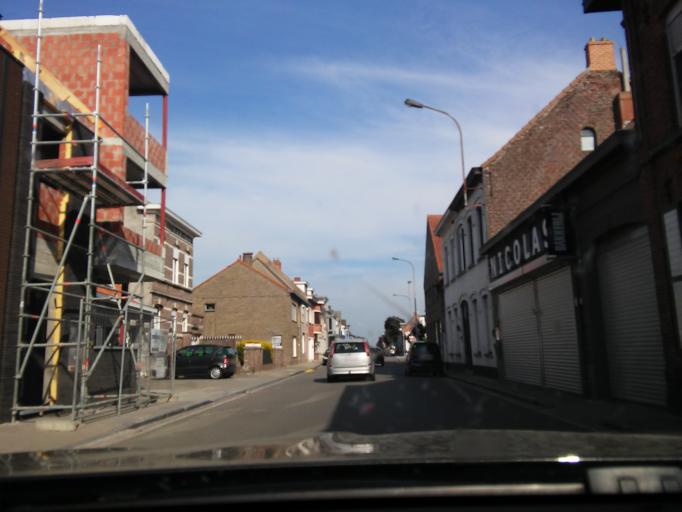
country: BE
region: Flanders
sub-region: Provincie Oost-Vlaanderen
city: Sint-Laureins
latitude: 51.2423
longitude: 3.5231
